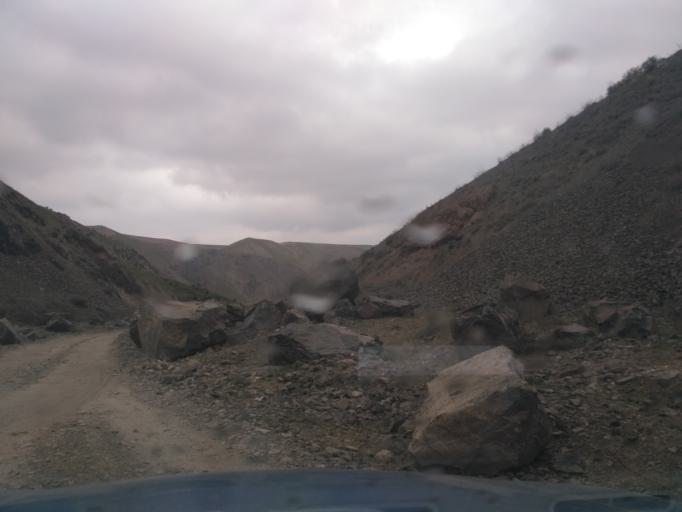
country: UZ
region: Jizzax
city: Zomin
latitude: 39.8606
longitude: 68.3843
